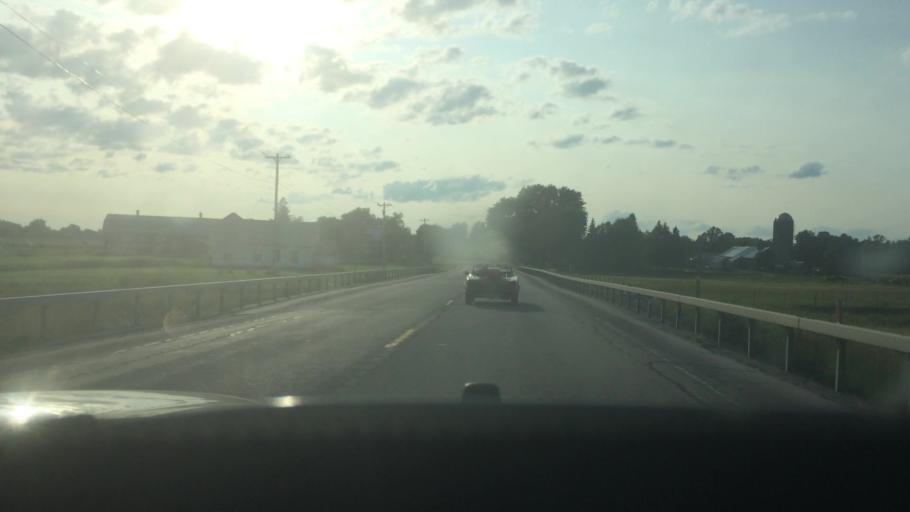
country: US
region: New York
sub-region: St. Lawrence County
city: Ogdensburg
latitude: 44.6638
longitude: -75.3462
